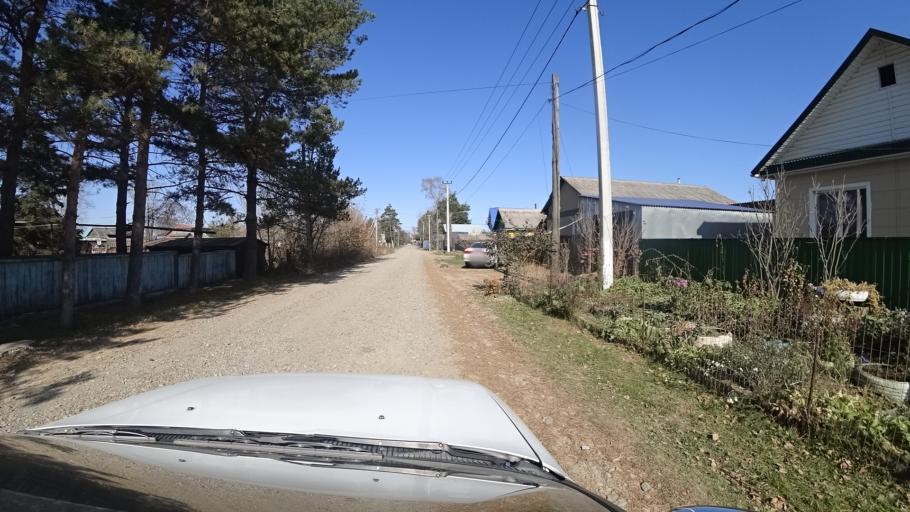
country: RU
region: Primorskiy
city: Dal'nerechensk
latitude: 45.9272
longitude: 133.7527
